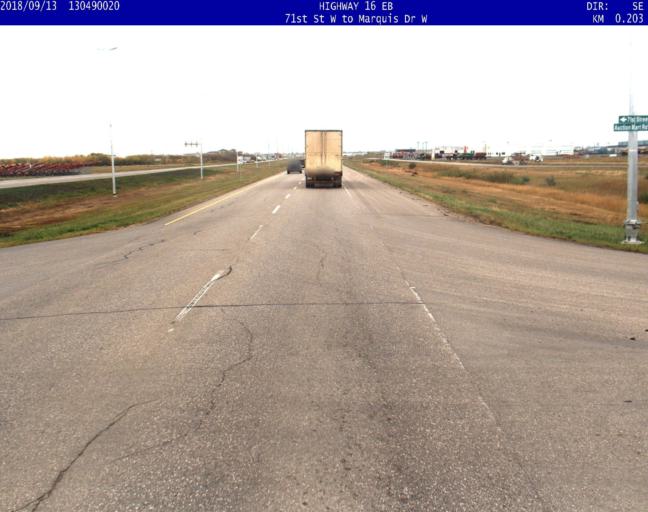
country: CA
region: Saskatchewan
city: Martensville
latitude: 52.2008
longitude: -106.7029
